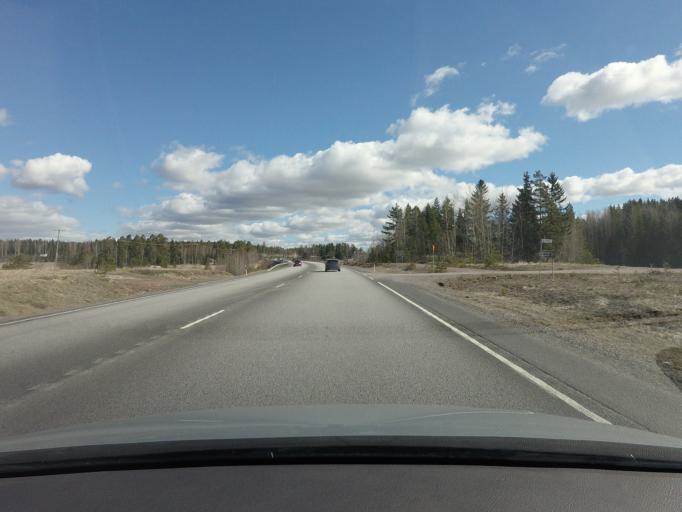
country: FI
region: Uusimaa
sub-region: Loviisa
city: Liljendal
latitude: 60.5986
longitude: 26.1110
